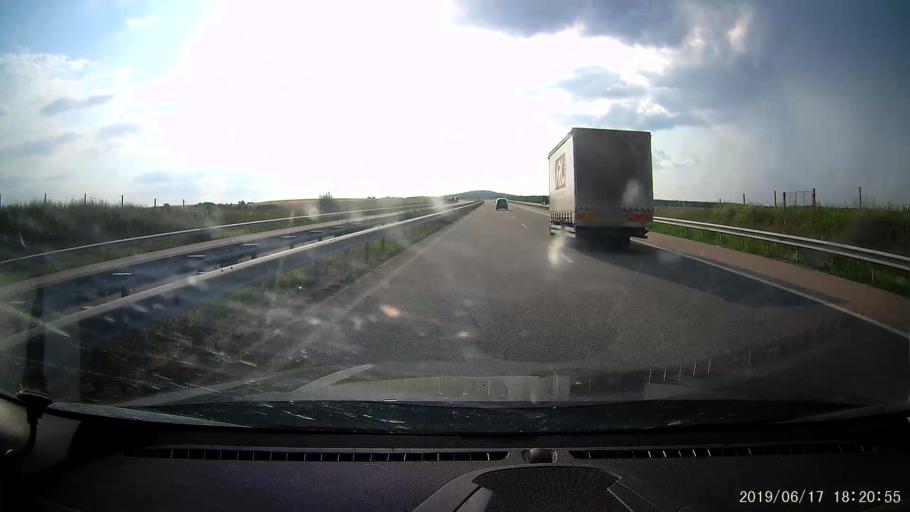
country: BG
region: Khaskovo
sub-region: Obshtina Simeonovgrad
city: Simeonovgrad
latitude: 41.9653
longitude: 25.7988
